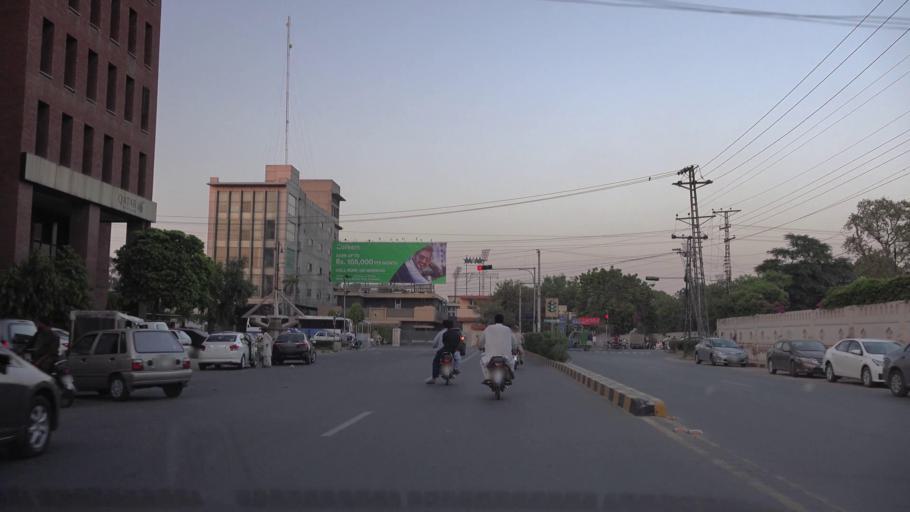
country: PK
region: Punjab
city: Faisalabad
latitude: 31.4301
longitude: 73.0809
